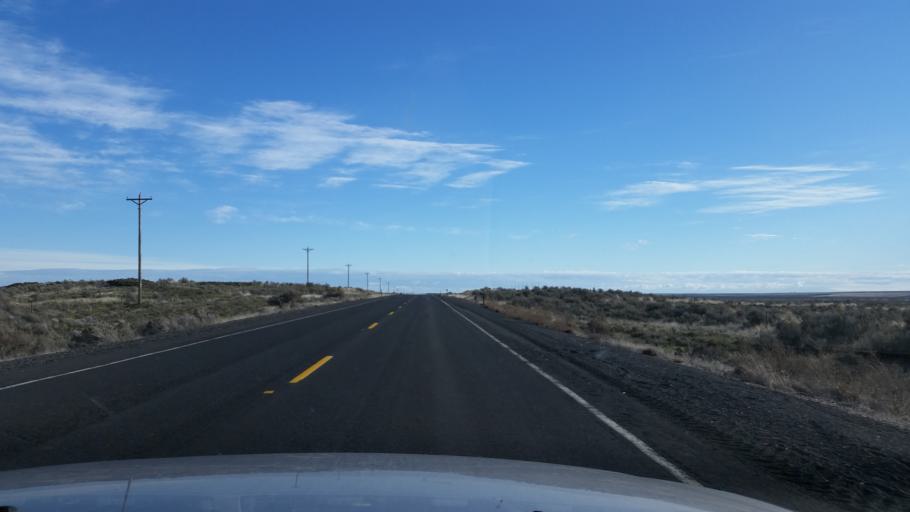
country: US
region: Washington
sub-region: Grant County
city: Warden
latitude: 47.3404
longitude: -118.9075
